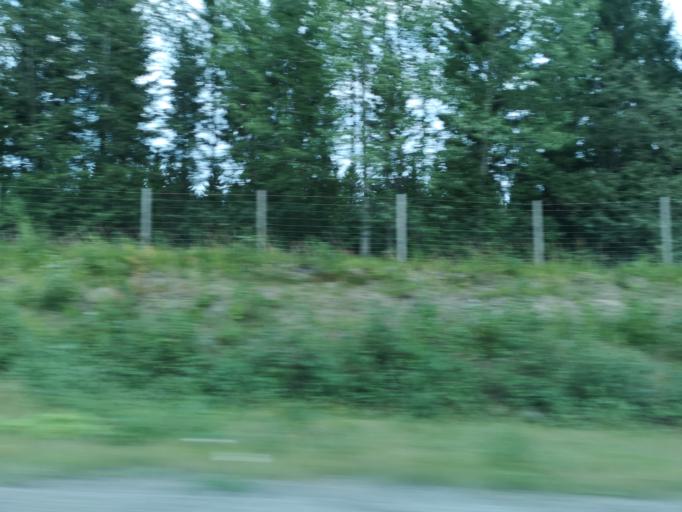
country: FI
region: Central Finland
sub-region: Jyvaeskylae
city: Toivakka
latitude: 62.0191
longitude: 26.0470
